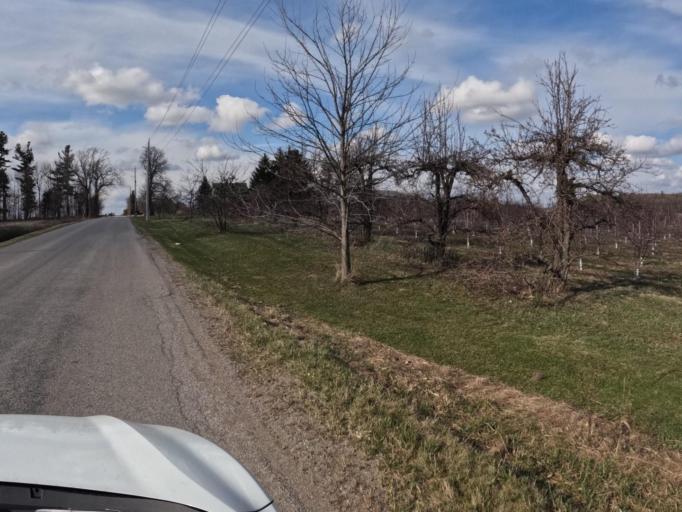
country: CA
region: Ontario
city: Norfolk County
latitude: 42.8650
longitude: -80.2755
